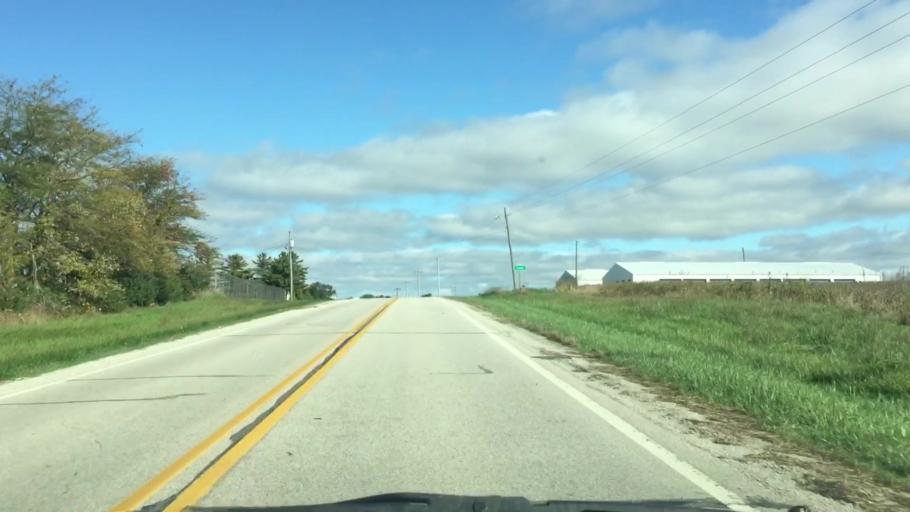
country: US
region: Iowa
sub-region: Decatur County
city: Leon
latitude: 40.7281
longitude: -93.7614
